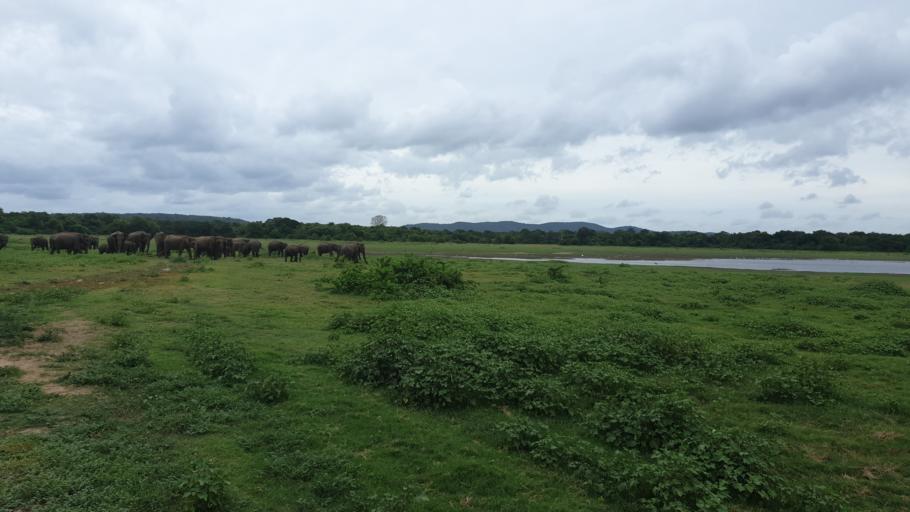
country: LK
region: North Central
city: Polonnaruwa
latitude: 8.1337
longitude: 80.9091
